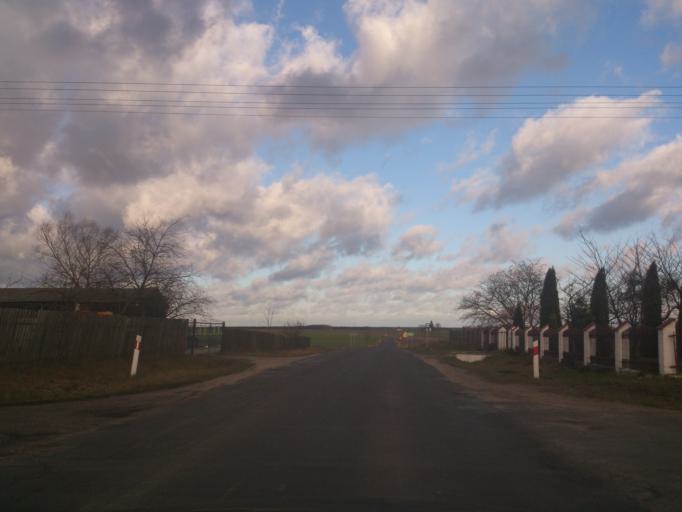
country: PL
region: Kujawsko-Pomorskie
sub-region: Powiat golubsko-dobrzynski
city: Ciechocin
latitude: 53.0308
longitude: 18.8852
